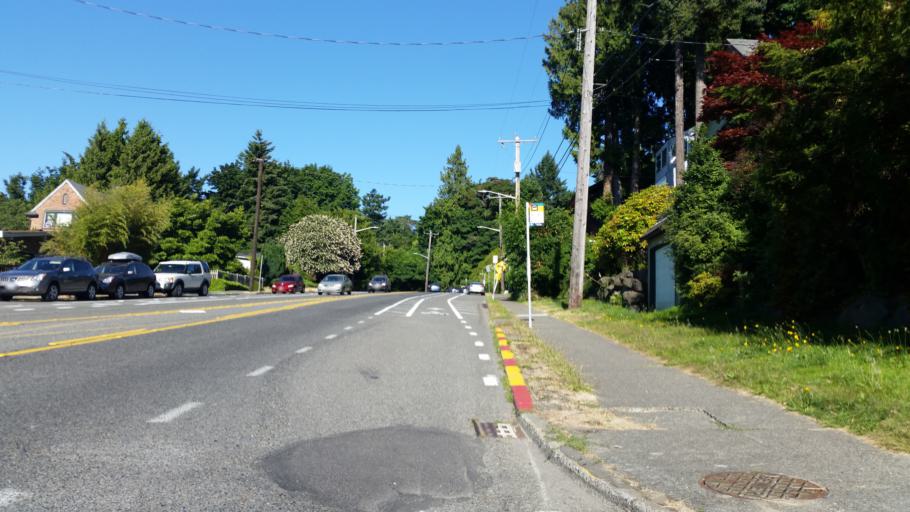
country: US
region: Washington
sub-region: King County
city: White Center
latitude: 47.5770
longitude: -122.4054
